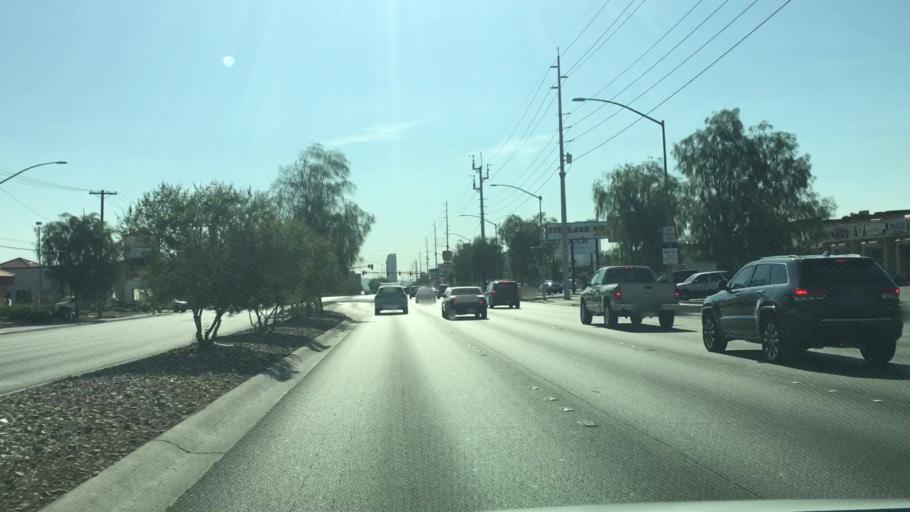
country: US
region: Nevada
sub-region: Clark County
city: Spring Valley
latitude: 36.1444
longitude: -115.1937
